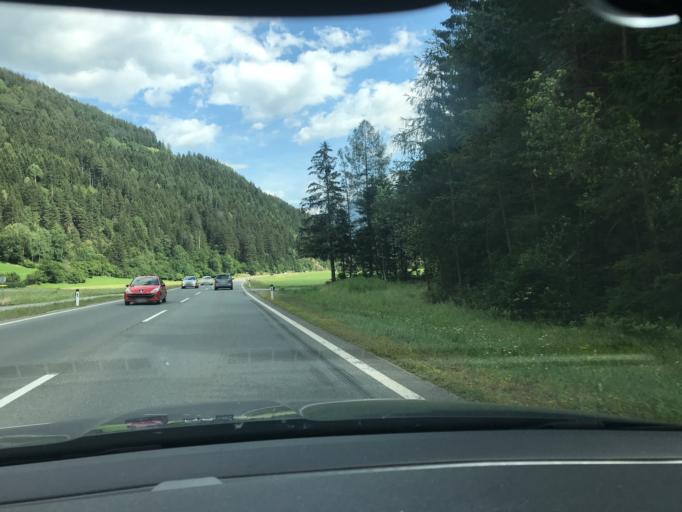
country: AT
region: Tyrol
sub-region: Politischer Bezirk Lienz
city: Ainet
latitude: 46.8578
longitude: 12.6979
